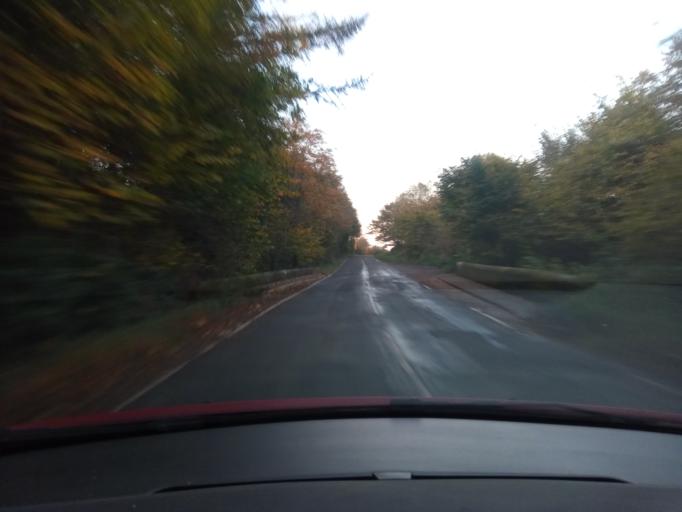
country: GB
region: England
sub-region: Northumberland
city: Bardon Mill
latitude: 54.9700
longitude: -2.2383
